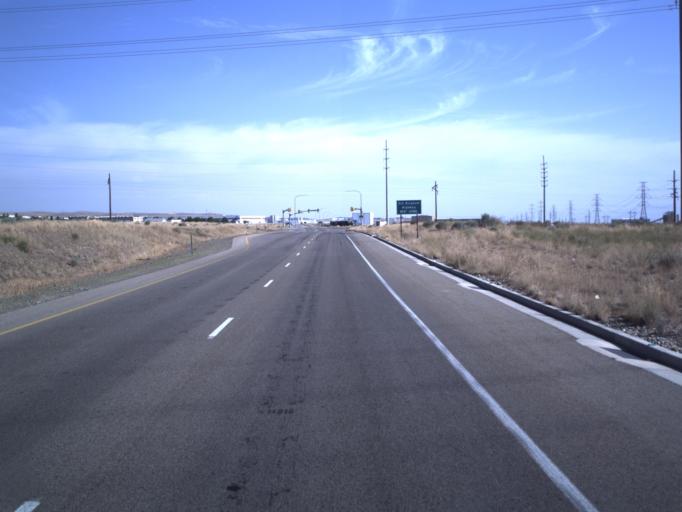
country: US
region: Utah
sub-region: Salt Lake County
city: Herriman
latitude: 40.5650
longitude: -112.0318
